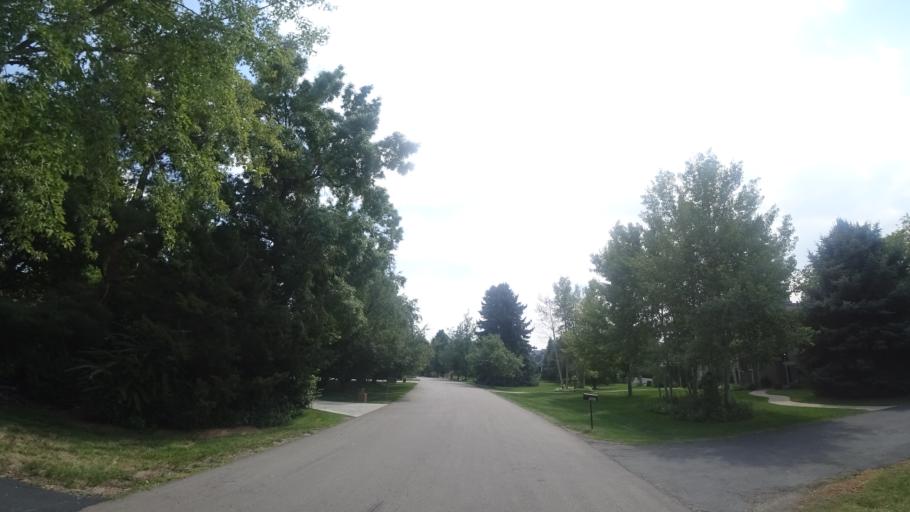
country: US
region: Colorado
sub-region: Arapahoe County
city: Greenwood Village
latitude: 39.6171
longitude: -104.9679
